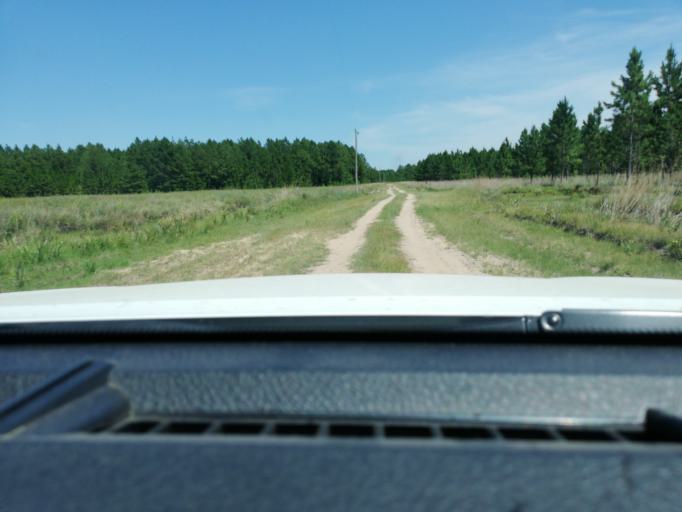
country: AR
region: Corrientes
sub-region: Departamento de San Miguel
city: San Miguel
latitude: -28.0285
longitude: -57.4735
